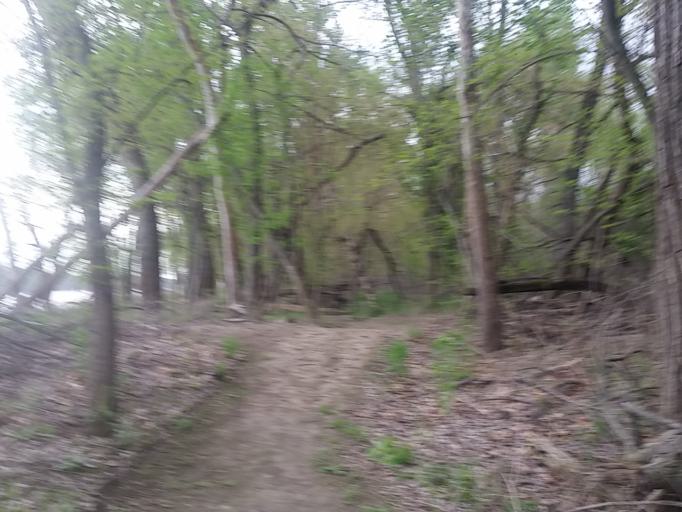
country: US
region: Nebraska
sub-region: Sarpy County
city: Bellevue
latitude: 41.1839
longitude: -95.8970
